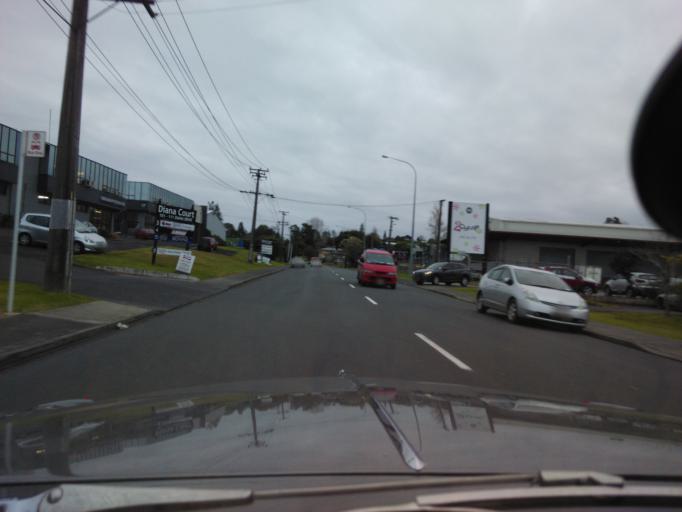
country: NZ
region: Auckland
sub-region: Auckland
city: North Shore
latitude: -36.7749
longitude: 174.7334
